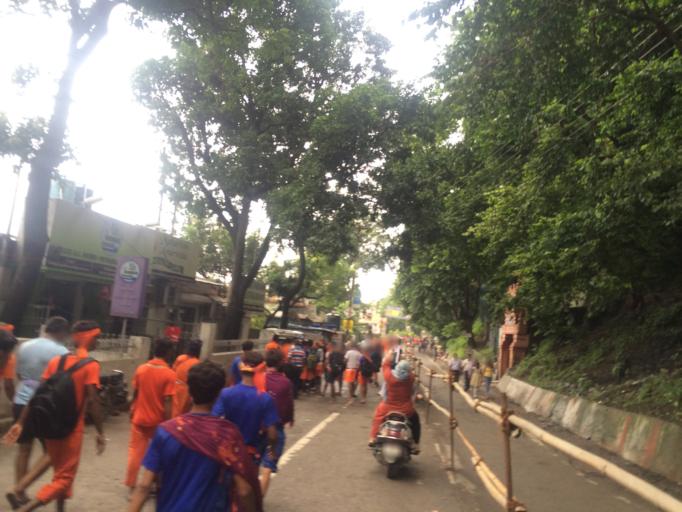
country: IN
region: Uttarakhand
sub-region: Dehradun
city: Rishikesh
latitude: 30.1226
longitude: 78.3102
